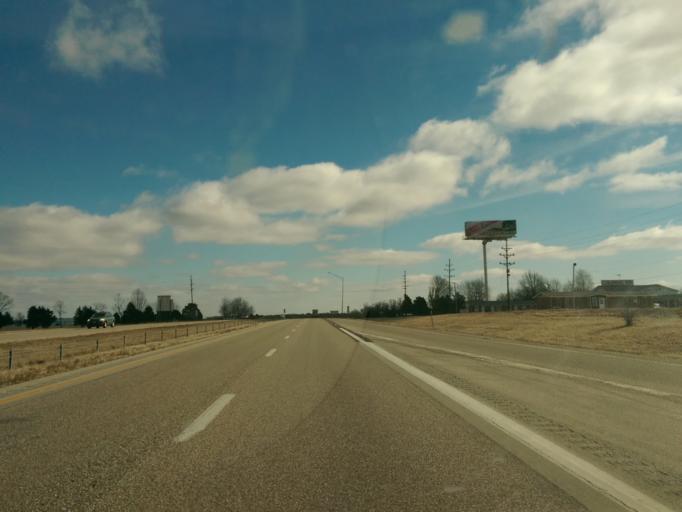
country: US
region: Missouri
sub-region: Montgomery County
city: Montgomery City
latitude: 38.8727
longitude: -91.3707
